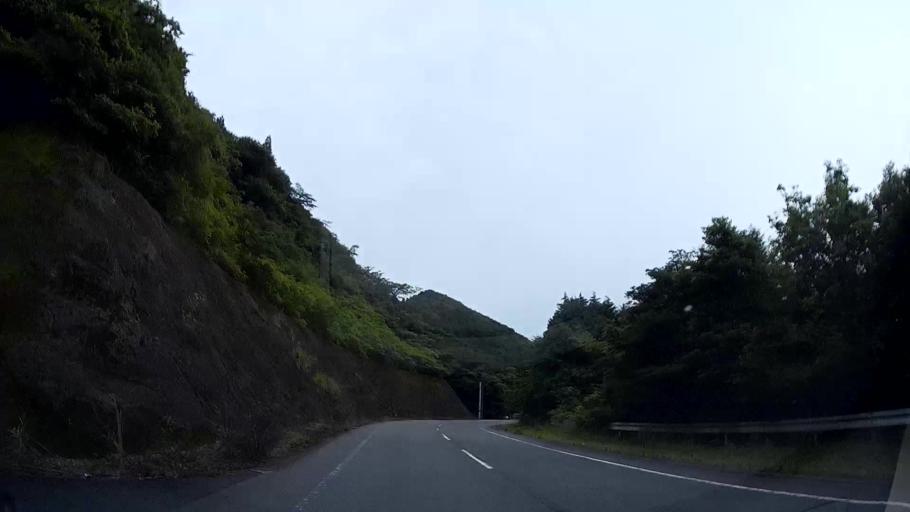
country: JP
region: Kumamoto
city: Kikuchi
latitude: 33.0538
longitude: 130.8996
